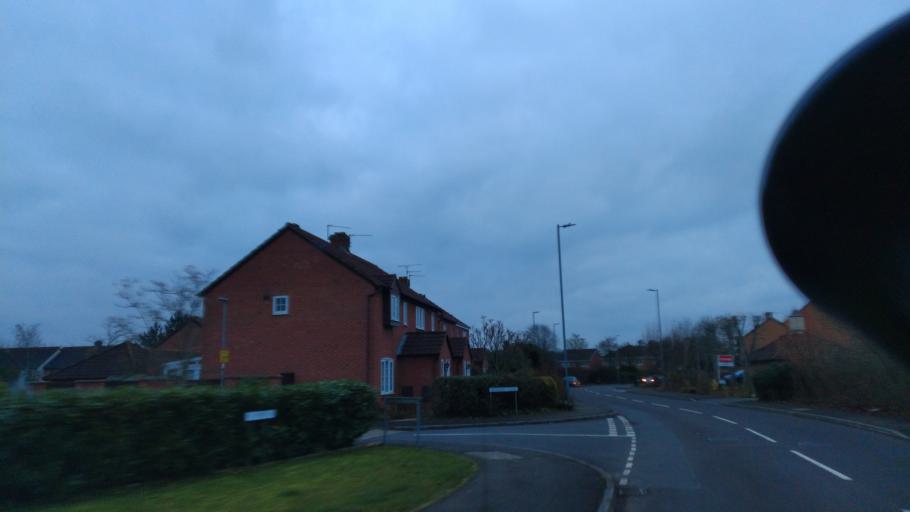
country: GB
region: England
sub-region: Wiltshire
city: Chippenham
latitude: 51.4510
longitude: -2.1462
